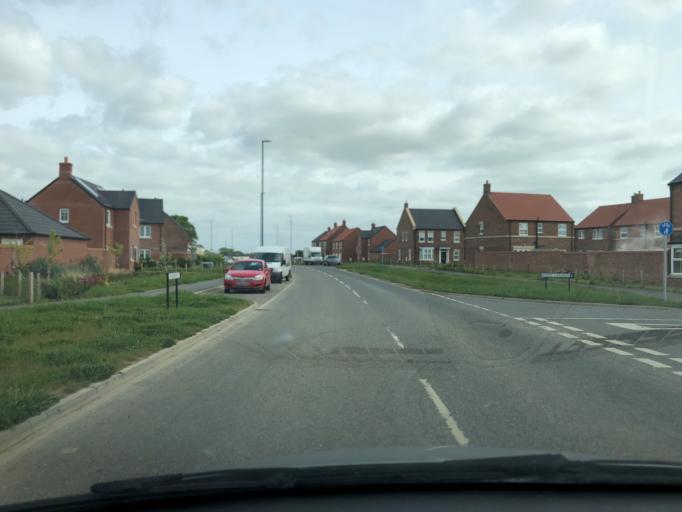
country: GB
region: England
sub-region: North Yorkshire
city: Thirsk
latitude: 54.2206
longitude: -1.3538
